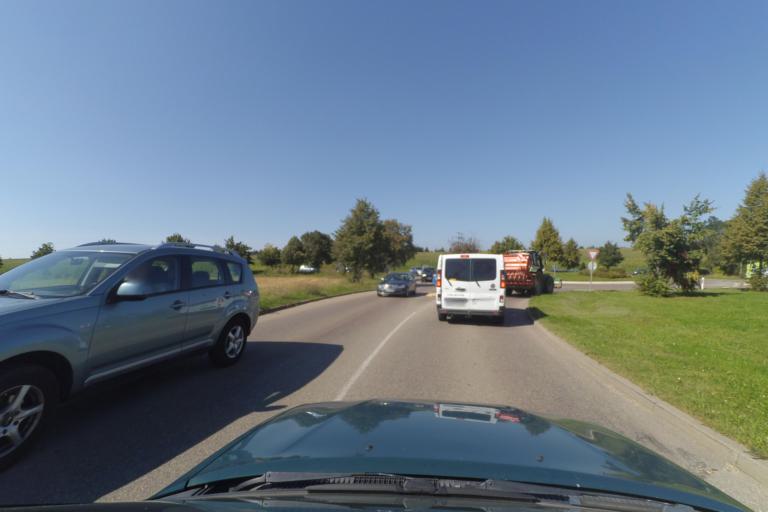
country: DE
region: Baden-Wuerttemberg
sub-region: Regierungsbezirk Stuttgart
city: Leinzell
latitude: 48.8426
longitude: 9.8632
